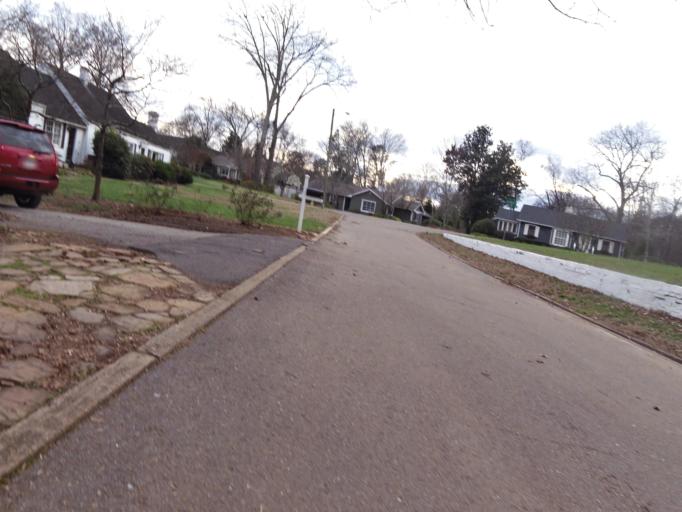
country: US
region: Tennessee
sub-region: Knox County
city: Knoxville
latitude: 35.9332
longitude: -83.9722
